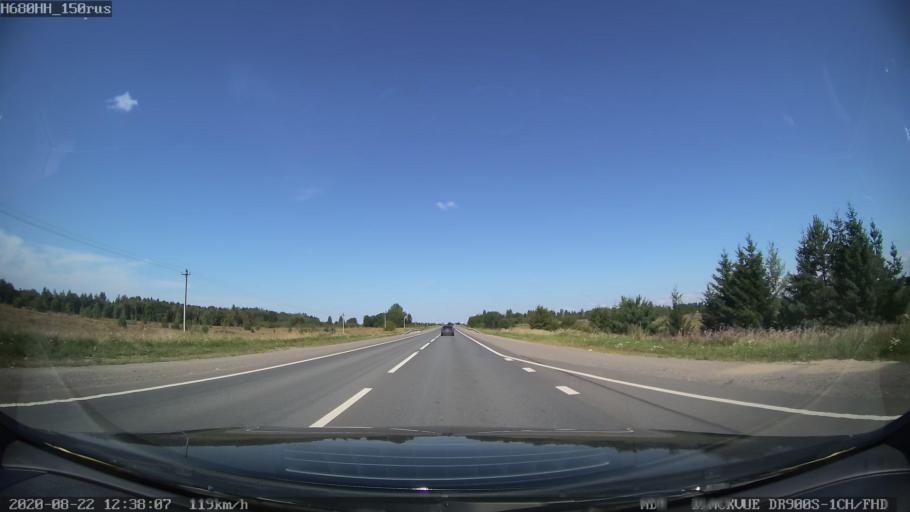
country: RU
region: Tverskaya
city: Rameshki
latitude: 57.3086
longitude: 36.0886
